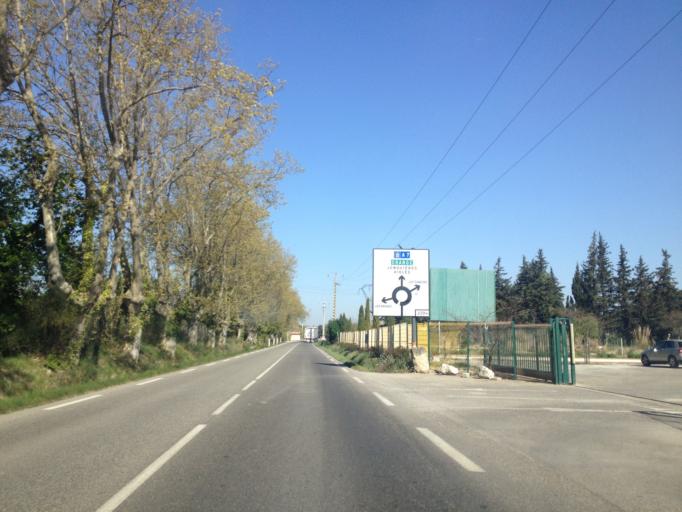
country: FR
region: Provence-Alpes-Cote d'Azur
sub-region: Departement du Vaucluse
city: Sarrians
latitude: 44.0956
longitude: 4.9479
